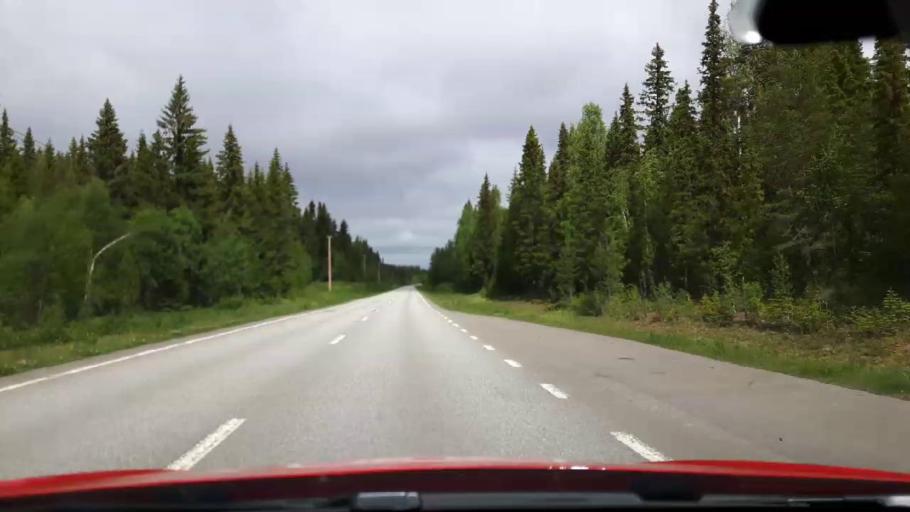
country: SE
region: Jaemtland
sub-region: Krokoms Kommun
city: Krokom
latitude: 63.4871
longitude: 14.5055
